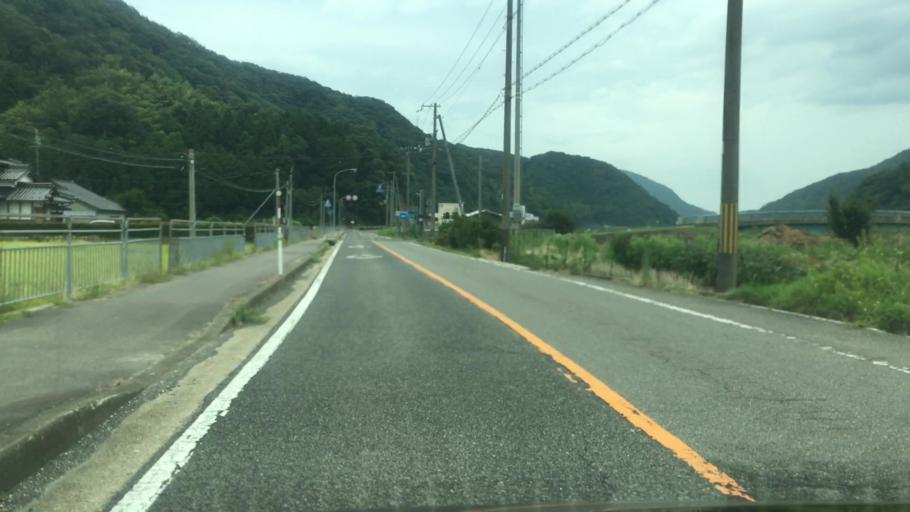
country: JP
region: Hyogo
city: Toyooka
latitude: 35.6330
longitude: 134.6806
